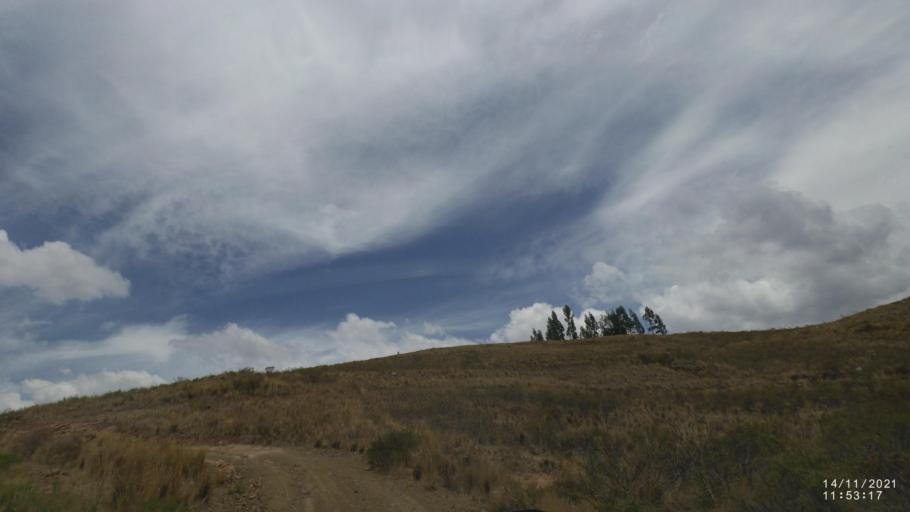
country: BO
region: Cochabamba
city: Colomi
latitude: -17.3639
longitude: -65.9810
